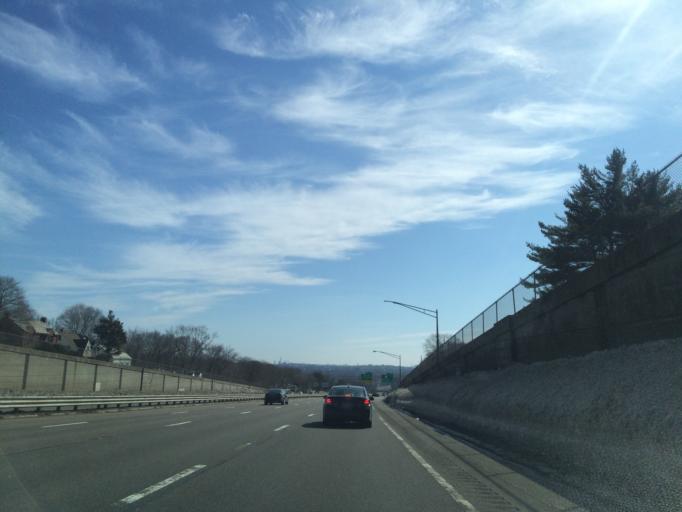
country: US
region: Massachusetts
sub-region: Middlesex County
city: Belmont
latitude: 42.4096
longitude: -71.1756
